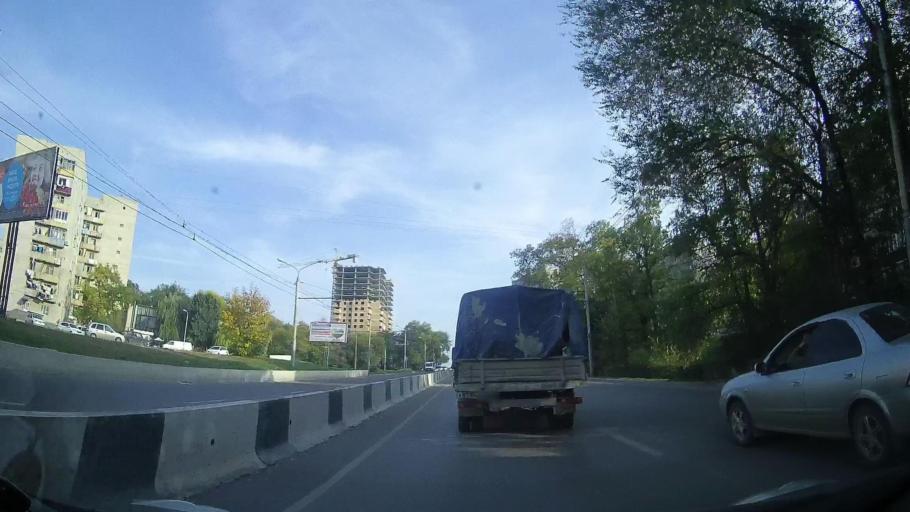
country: RU
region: Rostov
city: Temernik
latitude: 47.2888
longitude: 39.7407
